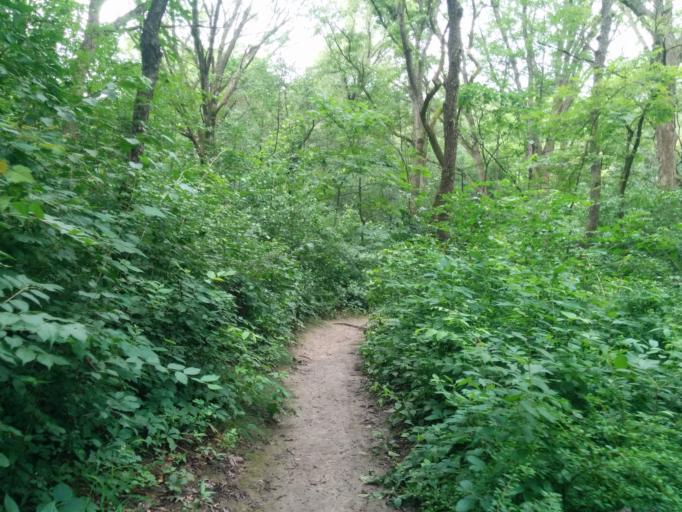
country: US
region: Illinois
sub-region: Cook County
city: Willow Springs
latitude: 41.7103
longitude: -87.8939
